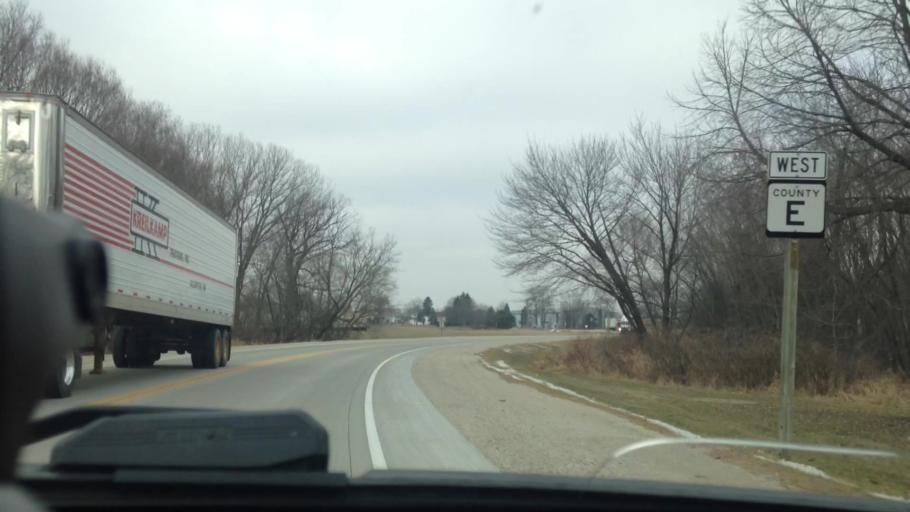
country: US
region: Wisconsin
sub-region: Dodge County
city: Horicon
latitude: 43.4515
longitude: -88.6428
